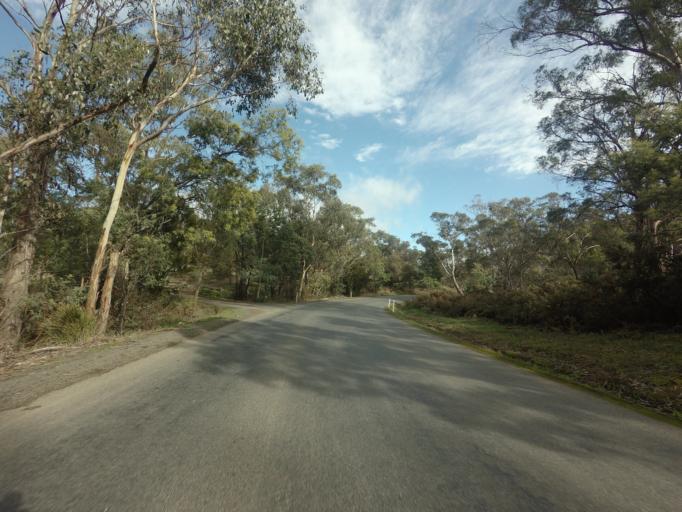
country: AU
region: Tasmania
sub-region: Derwent Valley
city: New Norfolk
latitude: -42.7803
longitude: 147.0148
